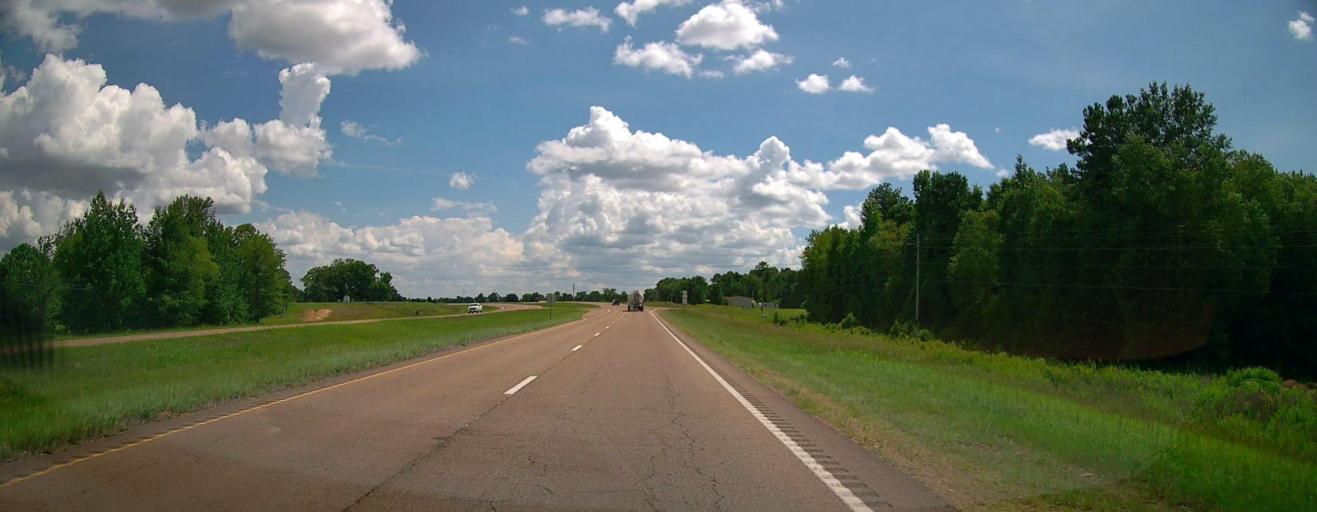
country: US
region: Mississippi
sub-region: Lowndes County
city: Columbus Air Force Base
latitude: 33.7171
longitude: -88.4504
